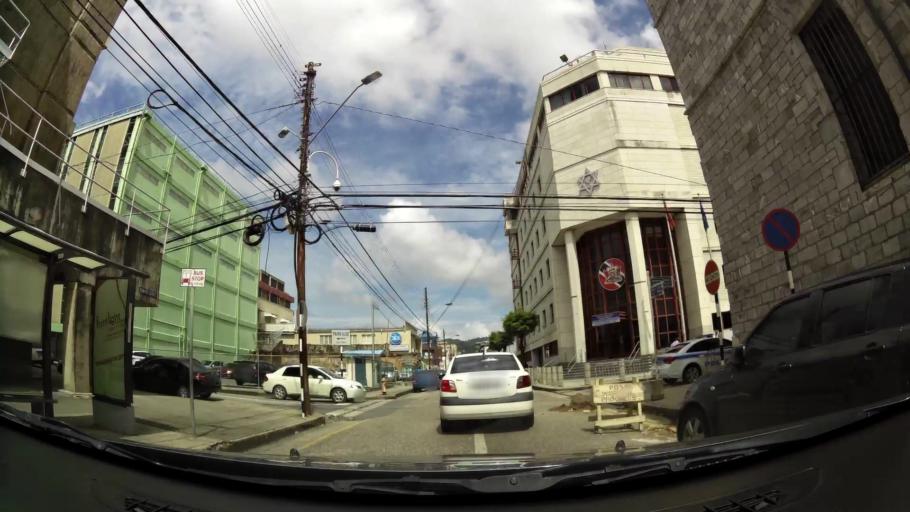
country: TT
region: San Juan/Laventille
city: Laventille
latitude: 10.6529
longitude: -61.5129
